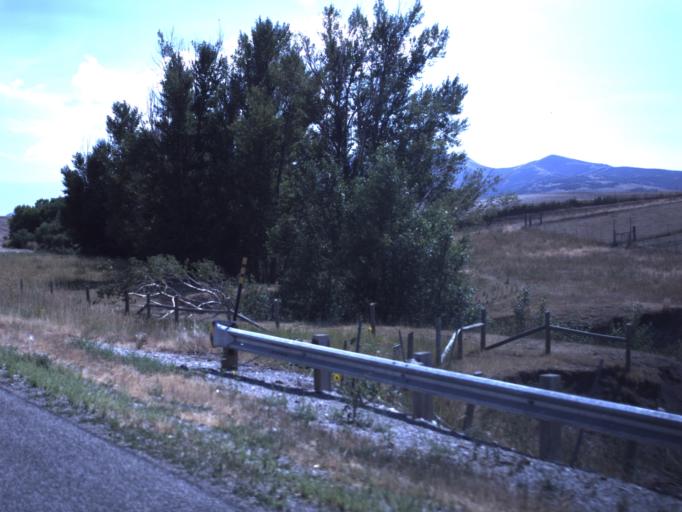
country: US
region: Utah
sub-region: Cache County
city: Mendon
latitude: 41.7838
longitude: -112.0258
